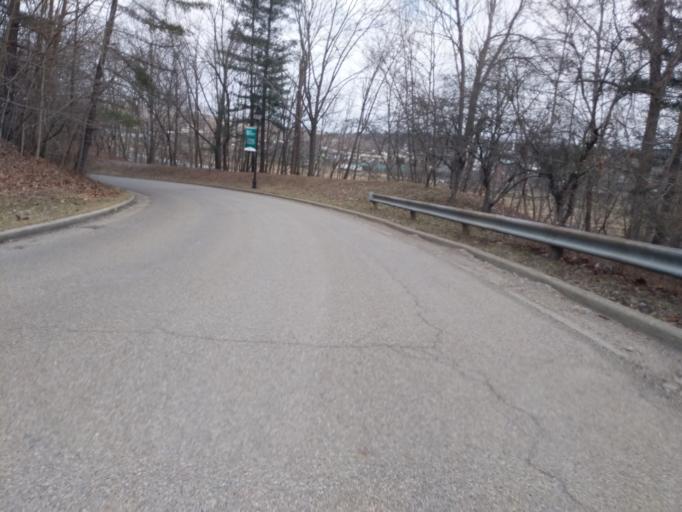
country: US
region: Ohio
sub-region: Athens County
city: Athens
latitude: 39.3218
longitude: -82.1104
